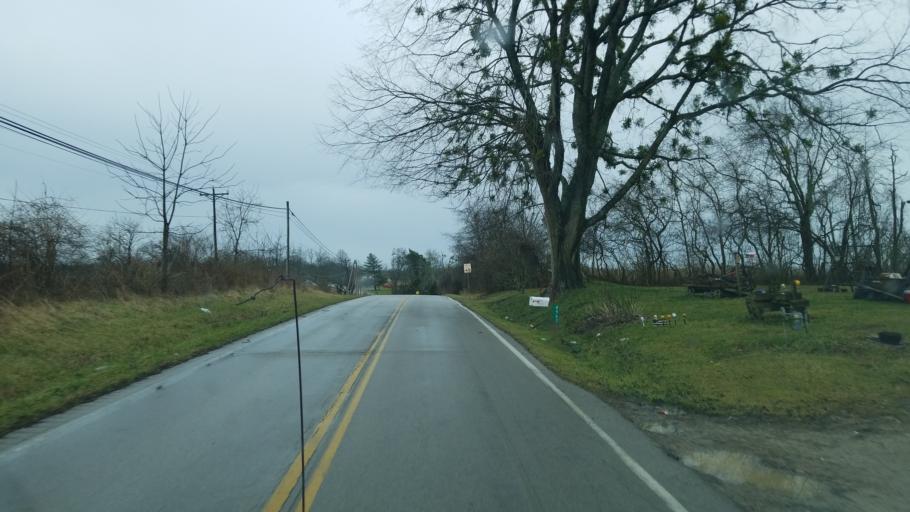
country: US
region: Kentucky
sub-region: Mason County
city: Maysville
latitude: 38.5944
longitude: -83.6706
